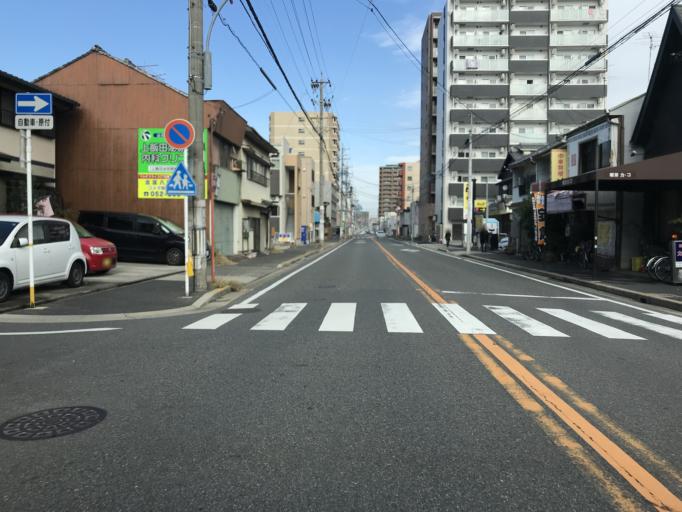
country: JP
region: Aichi
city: Nagoya-shi
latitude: 35.1925
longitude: 136.9244
